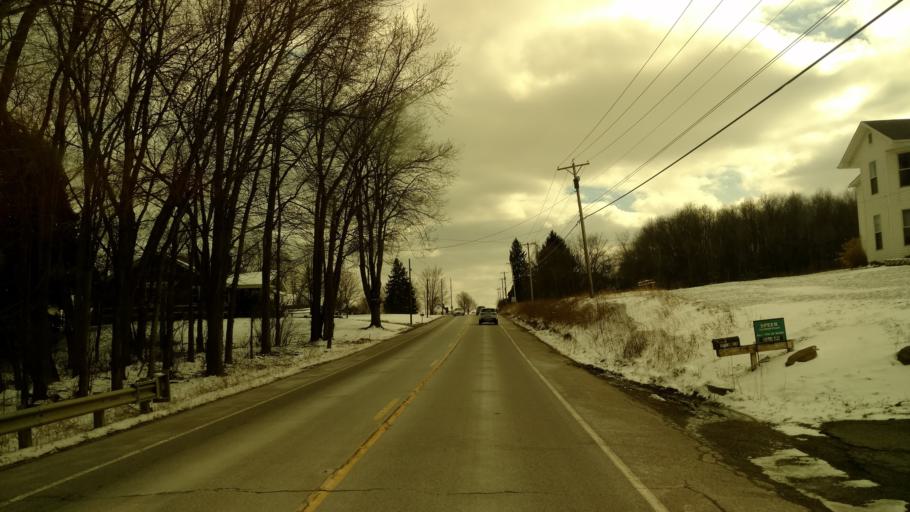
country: US
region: Pennsylvania
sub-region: Mercer County
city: Mercer
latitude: 41.2140
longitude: -80.2398
